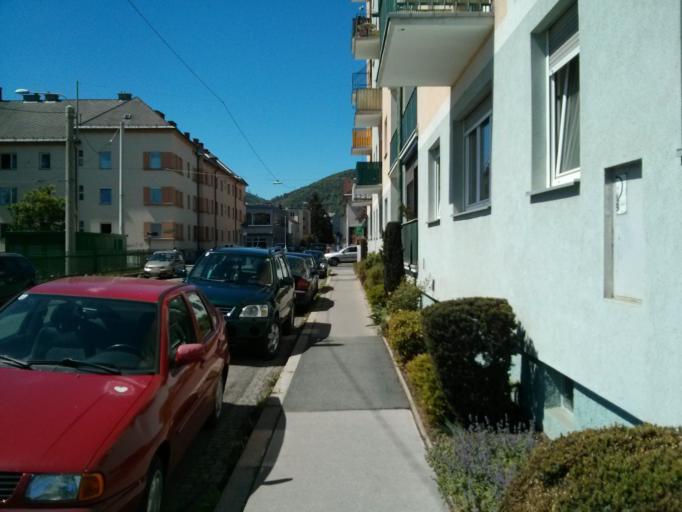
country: AT
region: Styria
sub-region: Graz Stadt
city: Wetzelsdorf
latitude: 47.0724
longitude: 15.4100
